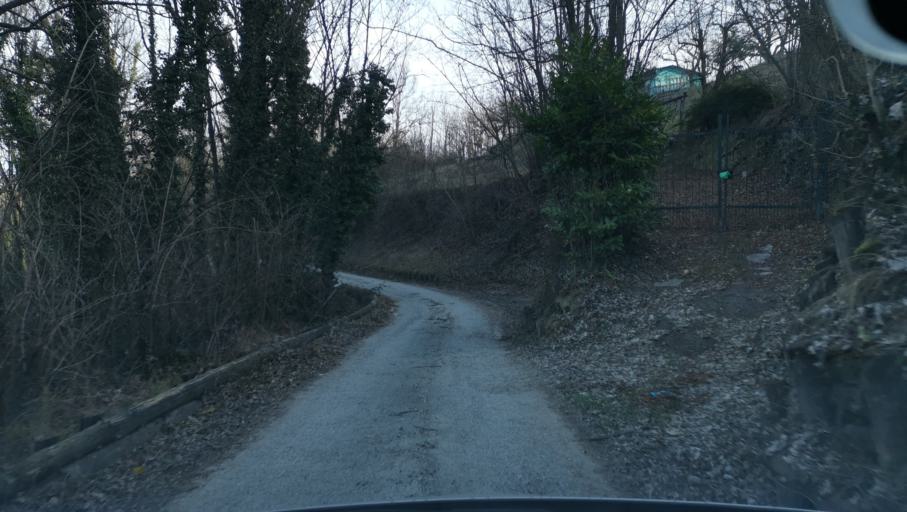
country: IT
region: Piedmont
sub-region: Provincia di Torino
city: Gassino Torinese
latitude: 45.1144
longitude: 7.8275
